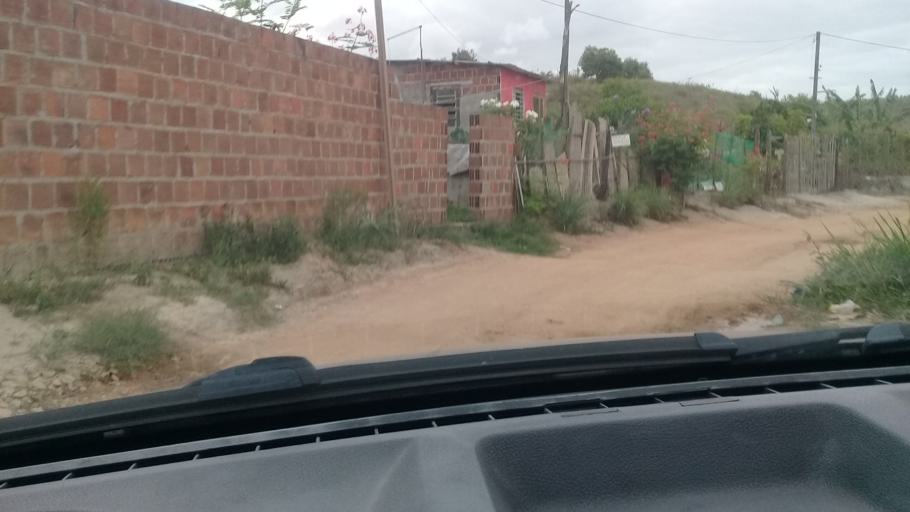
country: BR
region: Pernambuco
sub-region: Jaboatao Dos Guararapes
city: Jaboatao dos Guararapes
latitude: -8.0814
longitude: -35.0361
